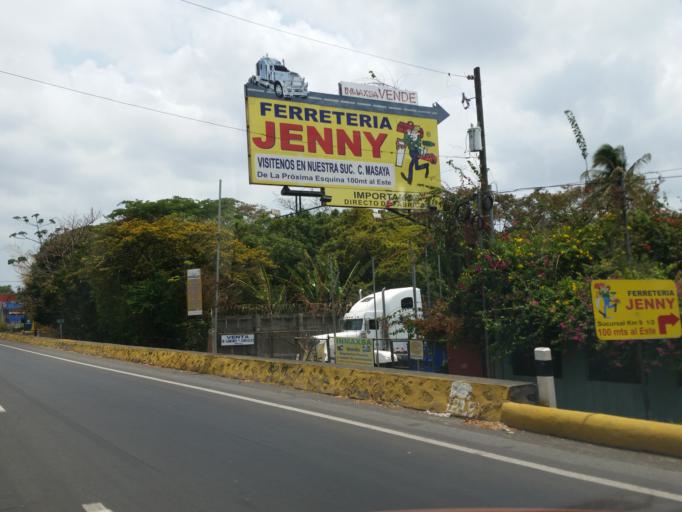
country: NI
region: Managua
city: Managua
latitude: 12.0869
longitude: -86.2312
